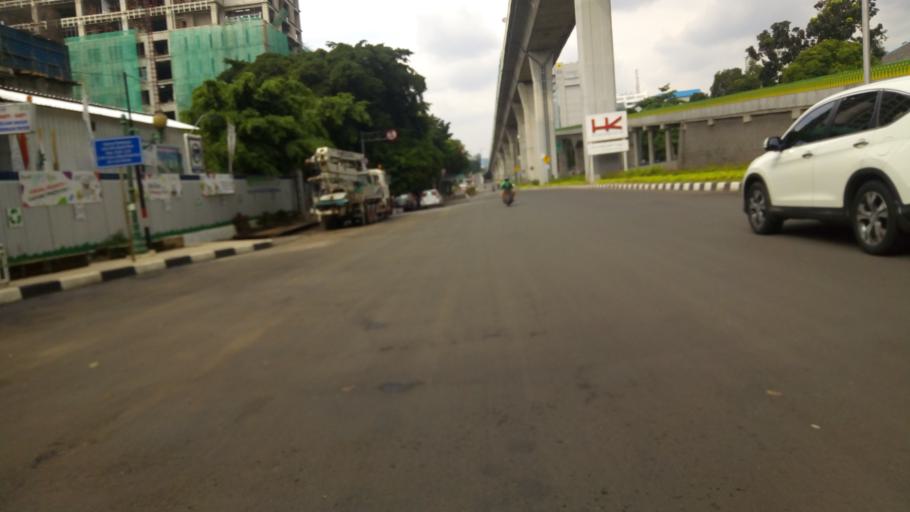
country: ID
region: Jakarta Raya
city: Jakarta
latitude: -6.2398
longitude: 106.7995
